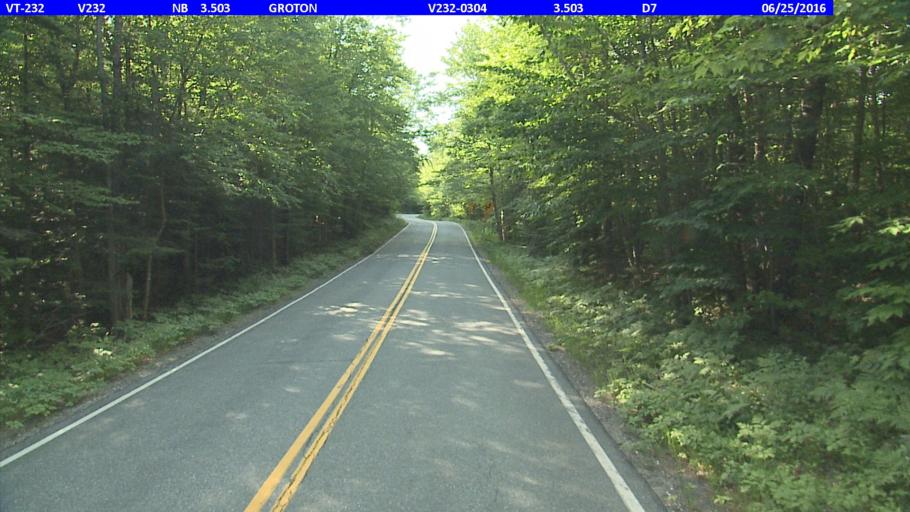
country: US
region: Vermont
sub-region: Washington County
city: Barre
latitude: 44.2542
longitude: -72.2684
